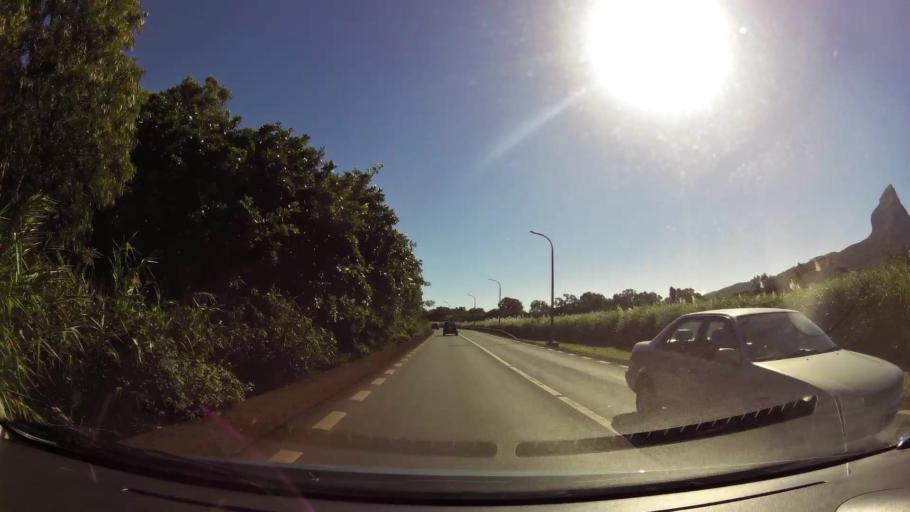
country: MU
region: Black River
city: Cascavelle
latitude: -20.3134
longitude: 57.4035
